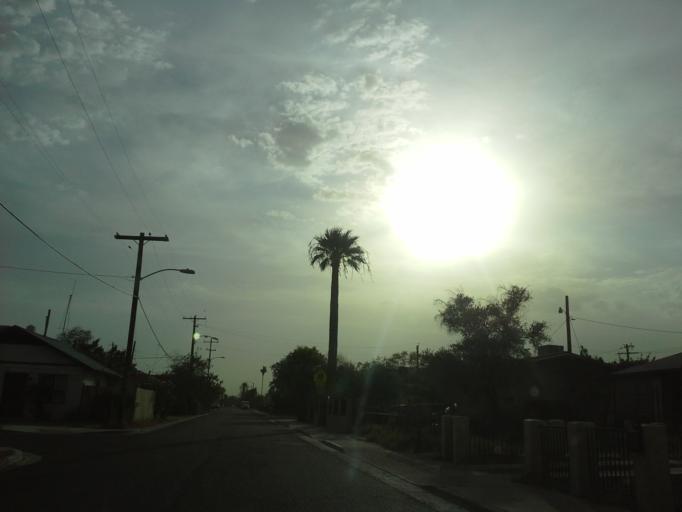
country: US
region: Arizona
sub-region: Maricopa County
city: Phoenix
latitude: 33.4532
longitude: -112.0927
